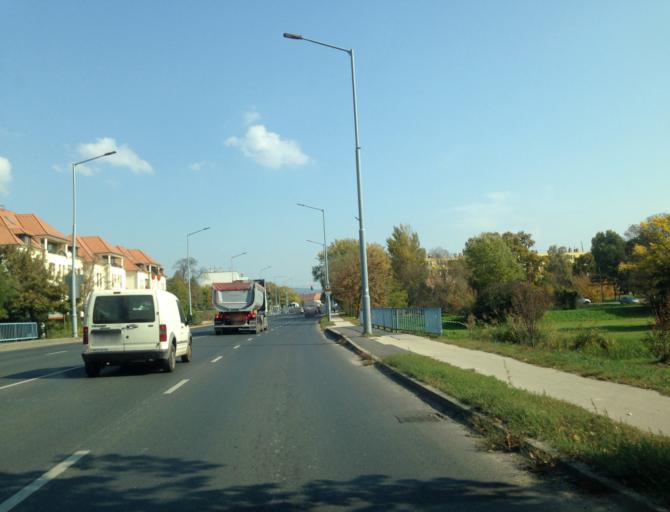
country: HU
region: Komarom-Esztergom
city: Tata
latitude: 47.6515
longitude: 18.3187
